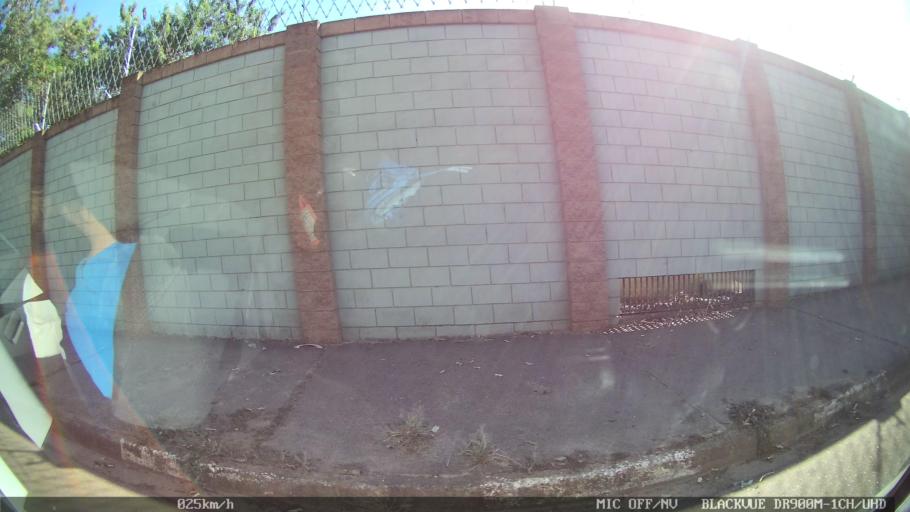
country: BR
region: Sao Paulo
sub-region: Sumare
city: Sumare
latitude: -22.8194
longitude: -47.2807
